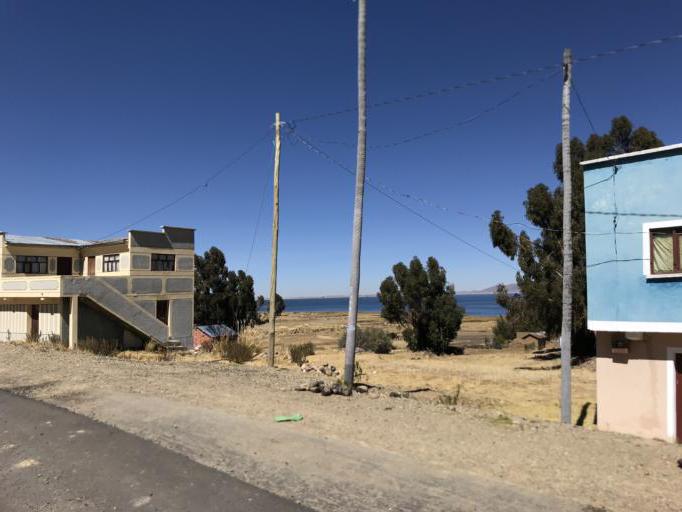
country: BO
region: La Paz
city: Huatajata
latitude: -16.2156
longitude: -68.6635
